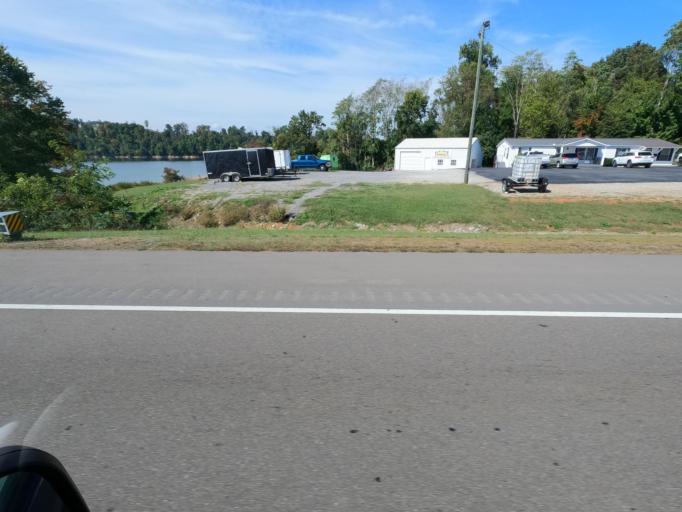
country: US
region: Tennessee
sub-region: Hamblen County
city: Morristown
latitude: 36.2699
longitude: -83.2843
